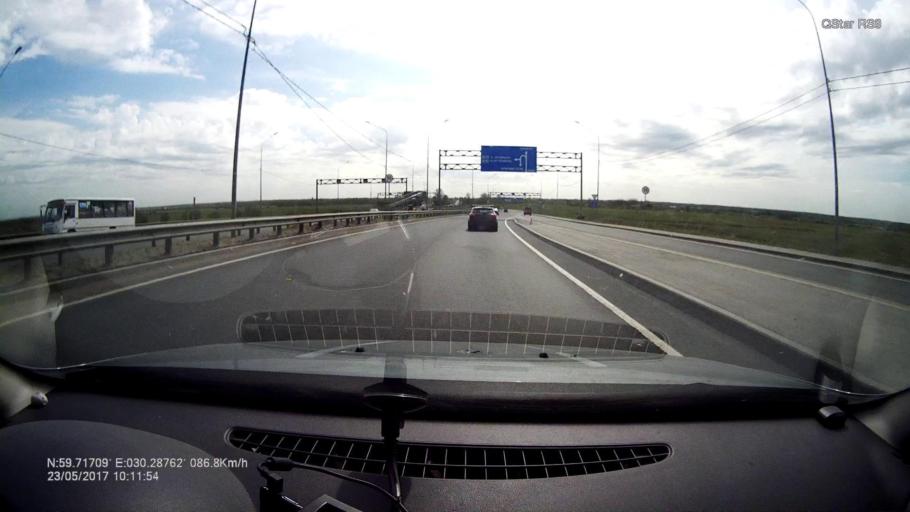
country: RU
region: St.-Petersburg
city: Aleksandrovskaya
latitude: 59.7170
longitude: 30.2881
